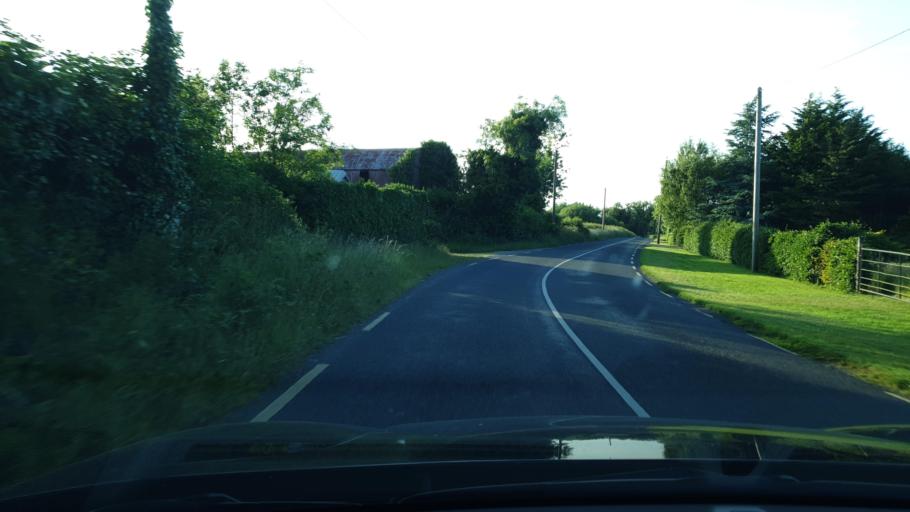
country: IE
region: Leinster
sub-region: An Mhi
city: Ratoath
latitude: 53.4974
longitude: -6.4405
